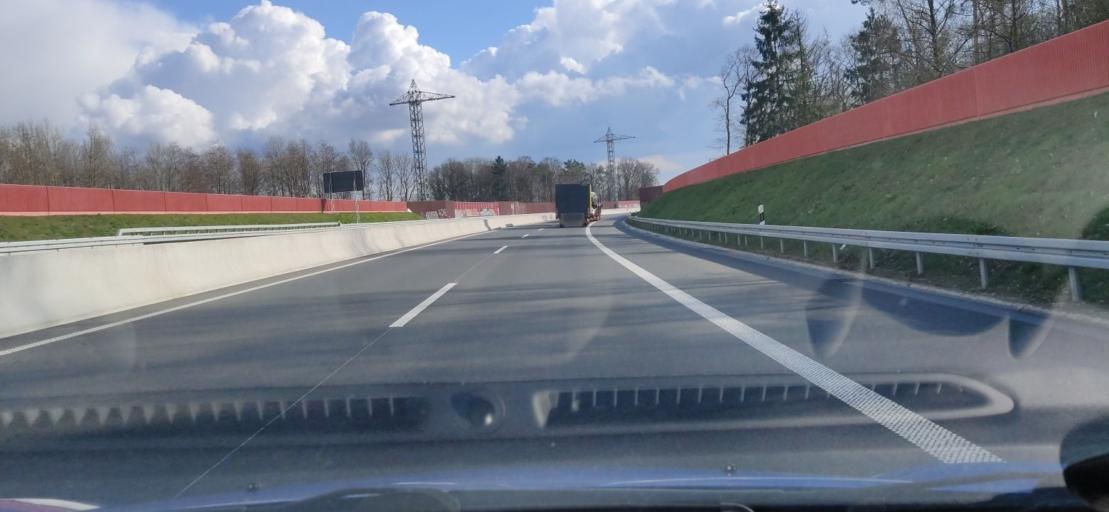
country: DE
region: North Rhine-Westphalia
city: Halle
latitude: 52.0569
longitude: 8.3371
